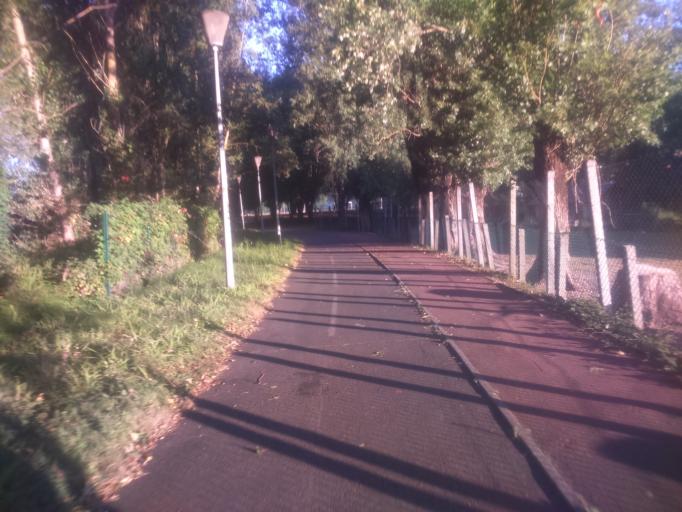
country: FR
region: Aquitaine
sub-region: Departement de la Gironde
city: Le Bouscat
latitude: 44.8709
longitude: -0.5688
